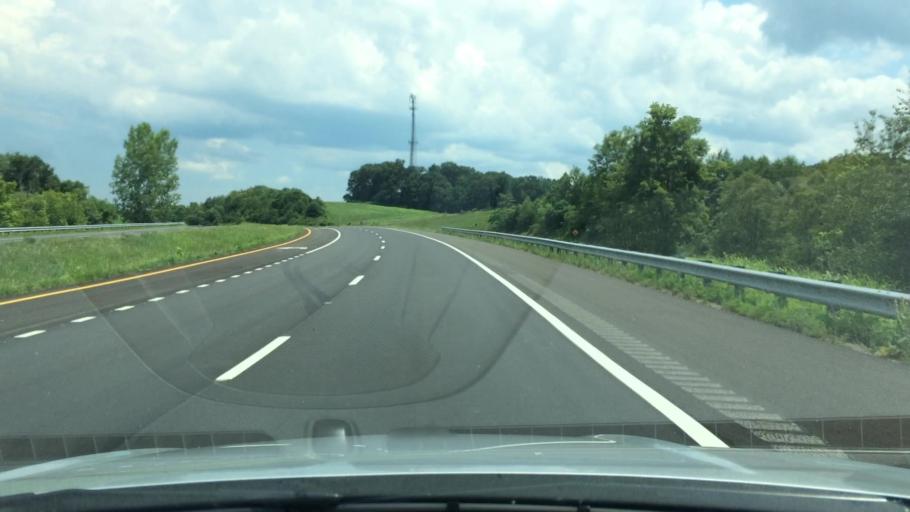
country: US
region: Tennessee
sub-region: Hamblen County
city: Morristown
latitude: 36.1728
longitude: -83.2301
